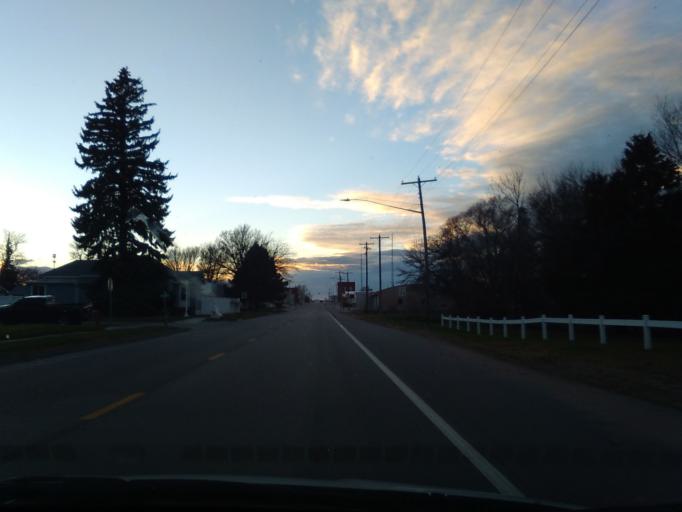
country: US
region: Nebraska
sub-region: Gosper County
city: Elwood
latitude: 40.5903
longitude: -99.8567
